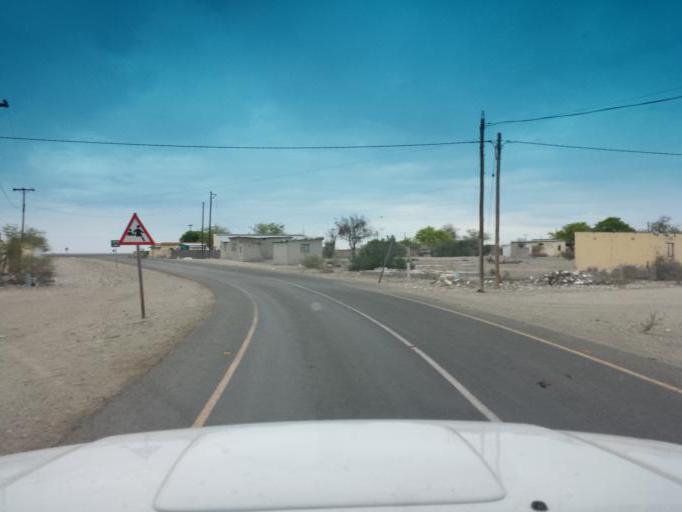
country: BW
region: Central
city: Mopipi
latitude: -21.2034
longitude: 24.8569
